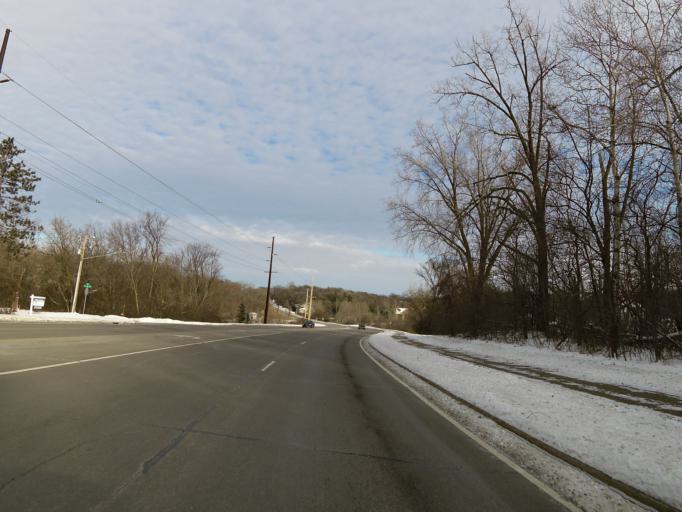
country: US
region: Minnesota
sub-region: Dakota County
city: Burnsville
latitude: 44.7206
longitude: -93.2987
